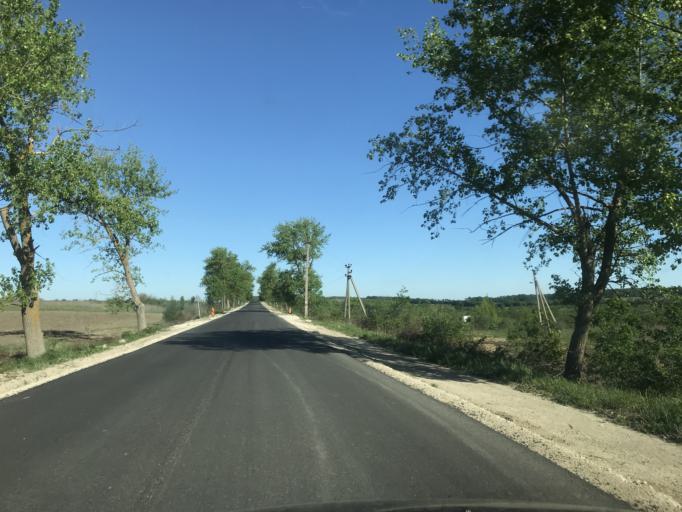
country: MD
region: Chisinau
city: Cricova
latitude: 47.2502
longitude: 28.8154
